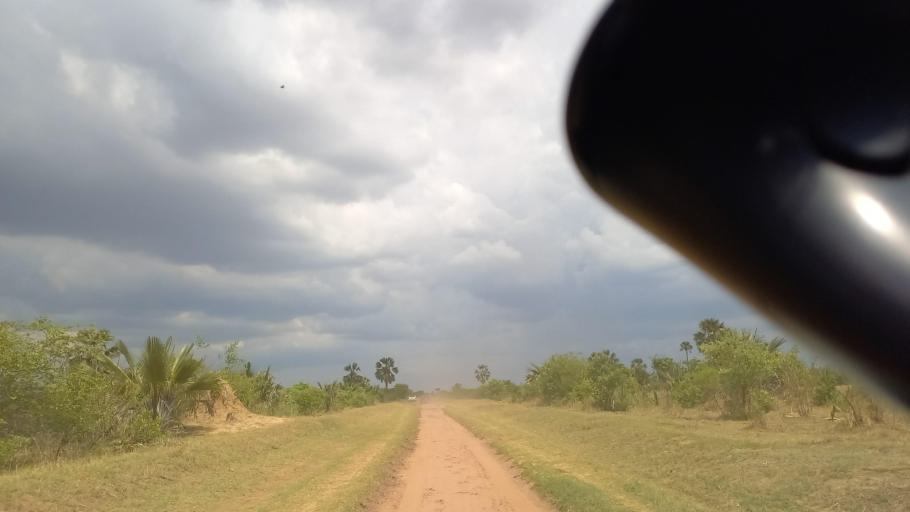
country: ZM
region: Lusaka
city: Kafue
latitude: -15.8331
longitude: 28.0693
